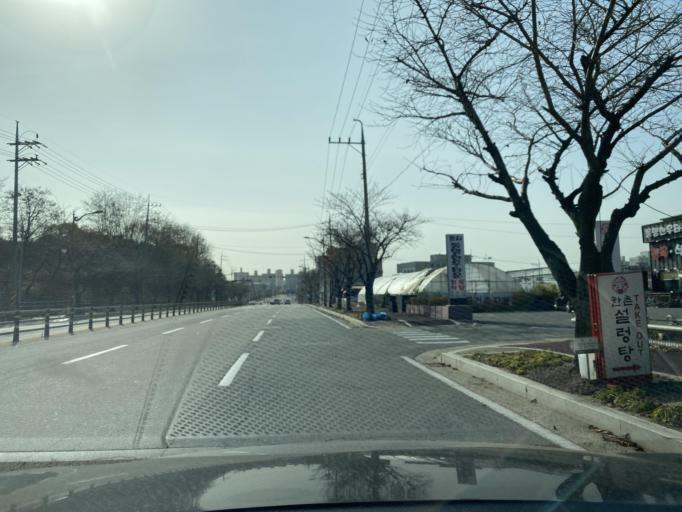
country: KR
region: Chungcheongnam-do
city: Yesan
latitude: 36.6956
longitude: 126.8368
